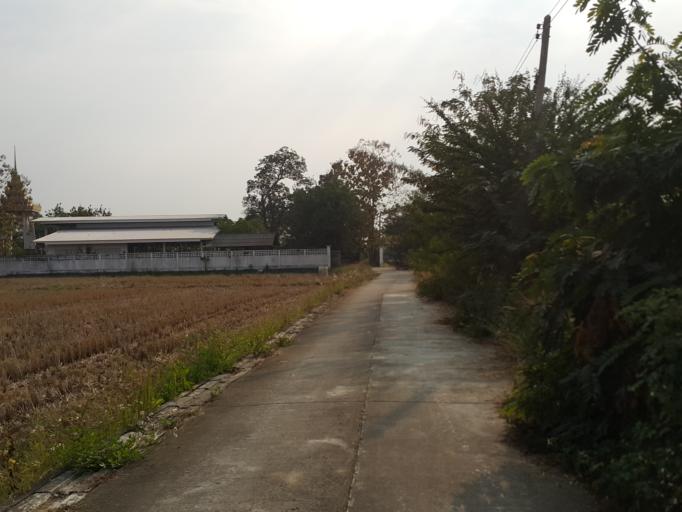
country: TH
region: Chiang Mai
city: San Kamphaeng
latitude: 18.7755
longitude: 99.0907
